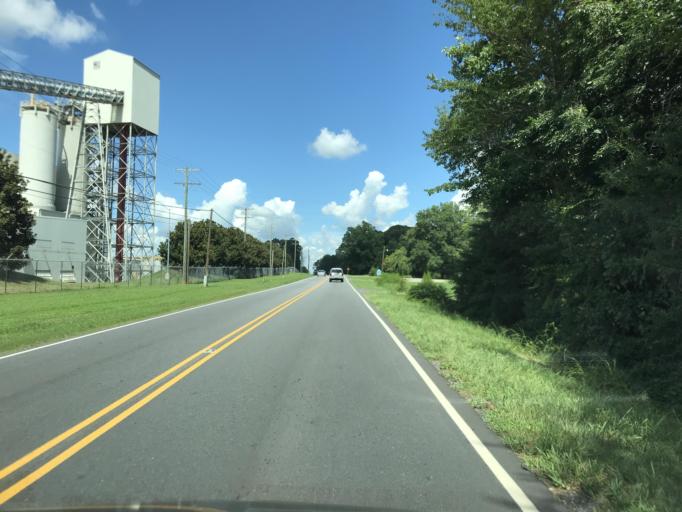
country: US
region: North Carolina
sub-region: Catawba County
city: Lake Norman of Catawba
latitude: 35.5958
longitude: -80.9618
